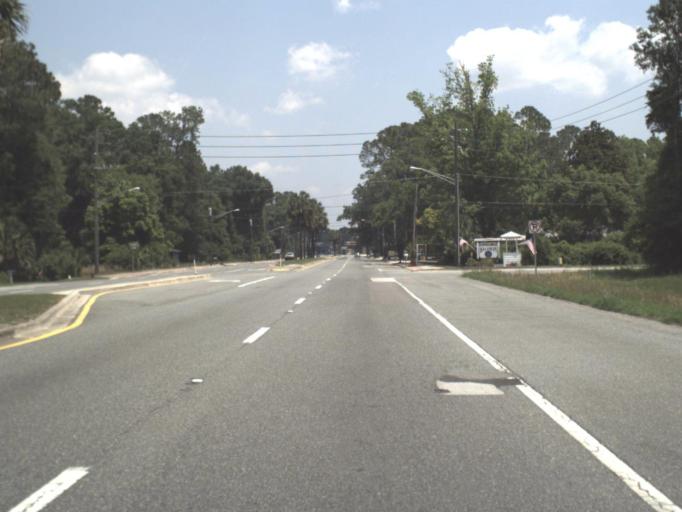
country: US
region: Florida
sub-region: Duval County
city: Baldwin
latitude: 30.2948
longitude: -81.9828
